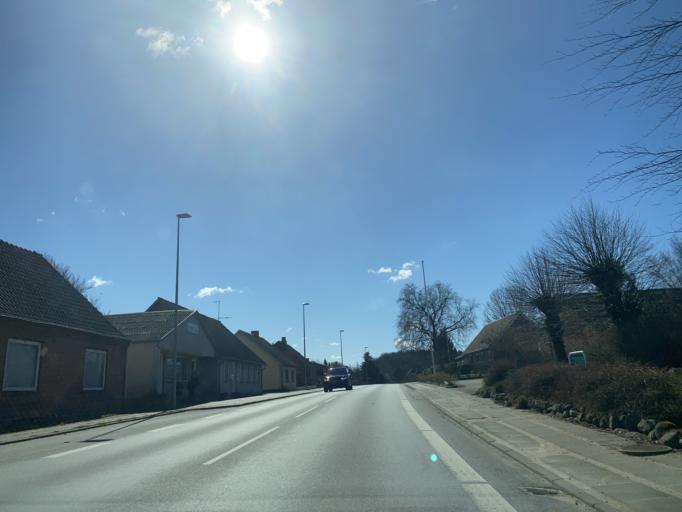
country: DK
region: Central Jutland
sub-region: Viborg Kommune
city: Bjerringbro
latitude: 56.2752
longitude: 9.6200
